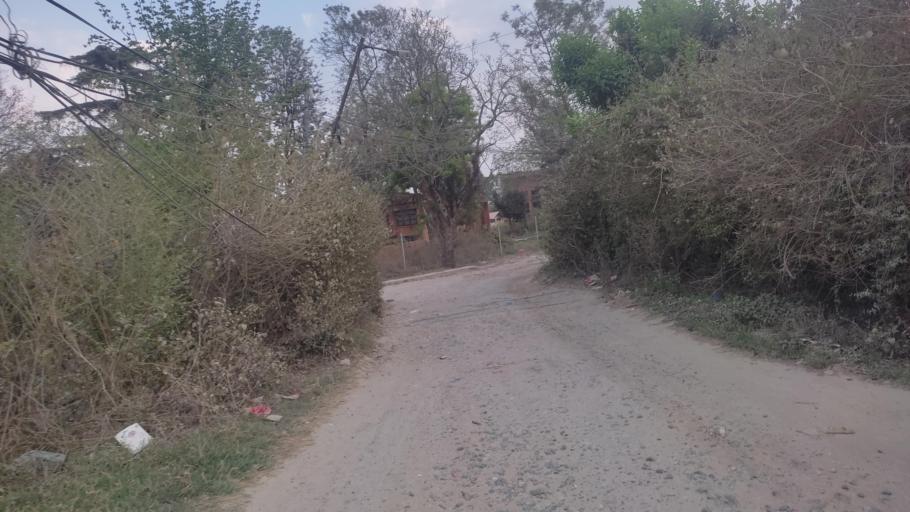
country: NP
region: Central Region
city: Kirtipur
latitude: 27.6842
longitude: 85.2835
